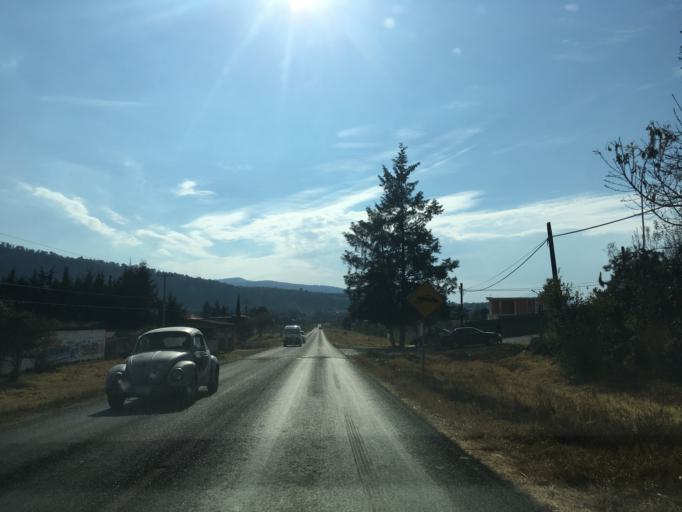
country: MX
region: Michoacan
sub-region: Patzcuaro
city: Santa Ana Chapitiro
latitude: 19.5339
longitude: -101.6409
